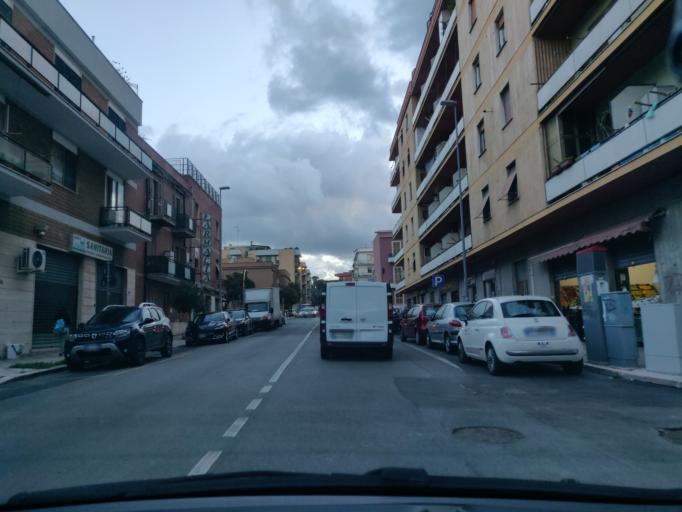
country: IT
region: Latium
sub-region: Citta metropolitana di Roma Capitale
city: Civitavecchia
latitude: 42.0959
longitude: 11.8022
